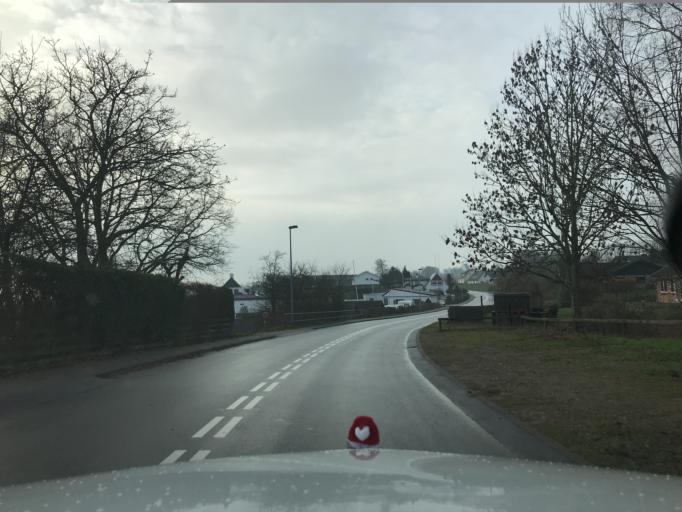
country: DK
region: South Denmark
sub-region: Sonderborg Kommune
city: Grasten
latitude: 54.9019
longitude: 9.5721
